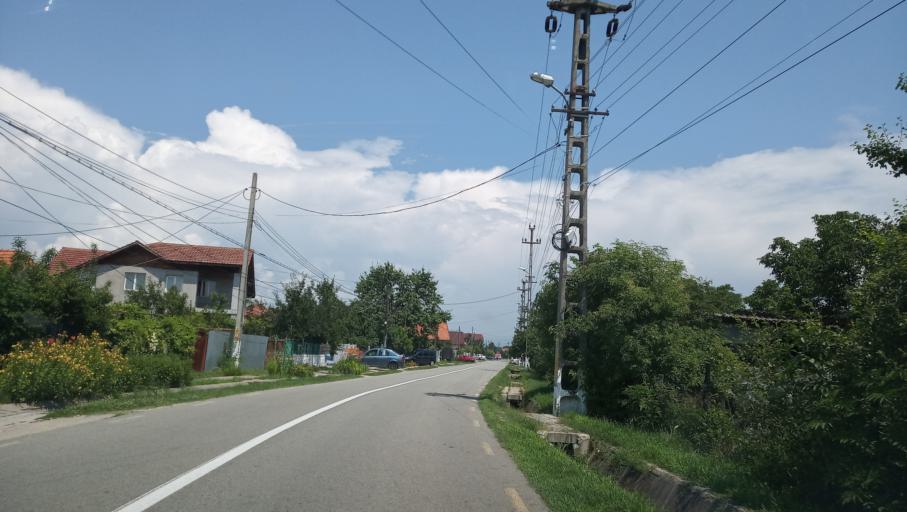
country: RO
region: Gorj
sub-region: Comuna Turcinesti
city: Turcinesti
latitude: 45.0546
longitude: 23.3470
